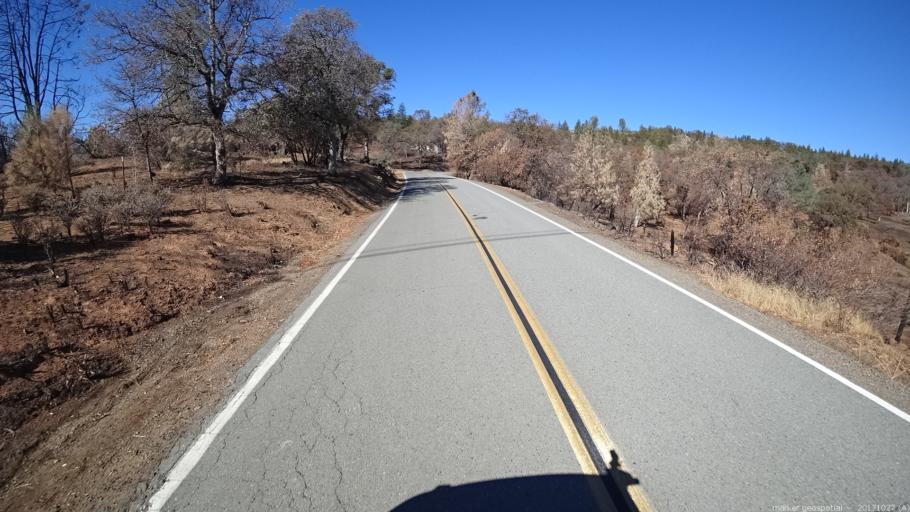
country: US
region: California
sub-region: Shasta County
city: Bella Vista
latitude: 40.7146
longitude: -122.0323
